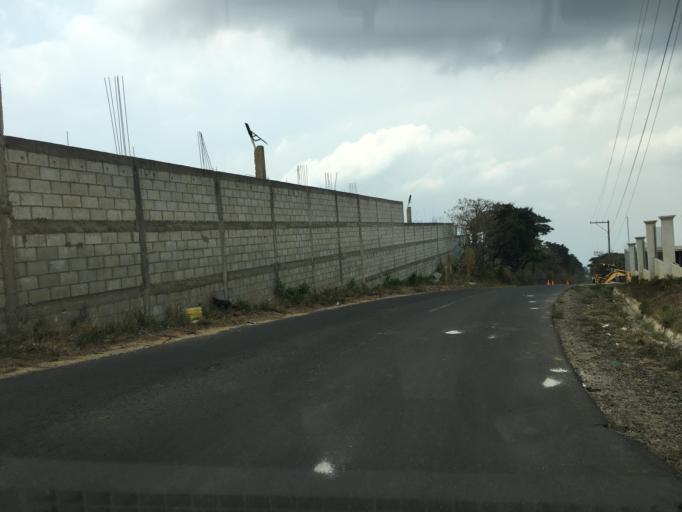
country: GT
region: Escuintla
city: San Vicente Pacaya
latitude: 14.3361
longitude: -90.5656
